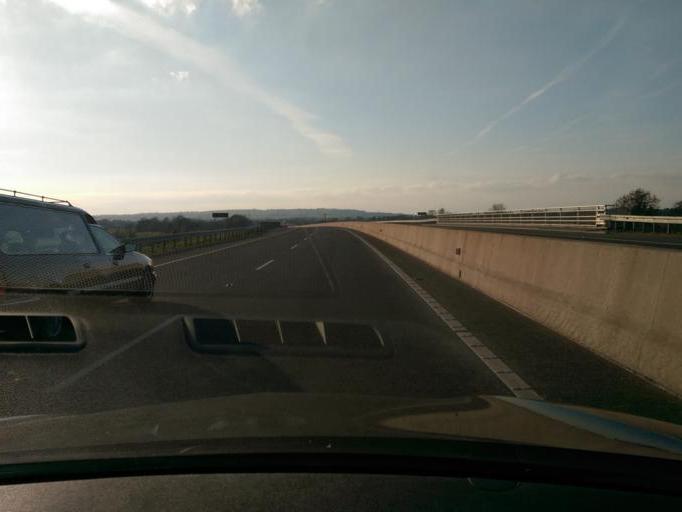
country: IE
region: Munster
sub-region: North Tipperary
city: Roscrea
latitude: 52.9234
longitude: -7.7330
